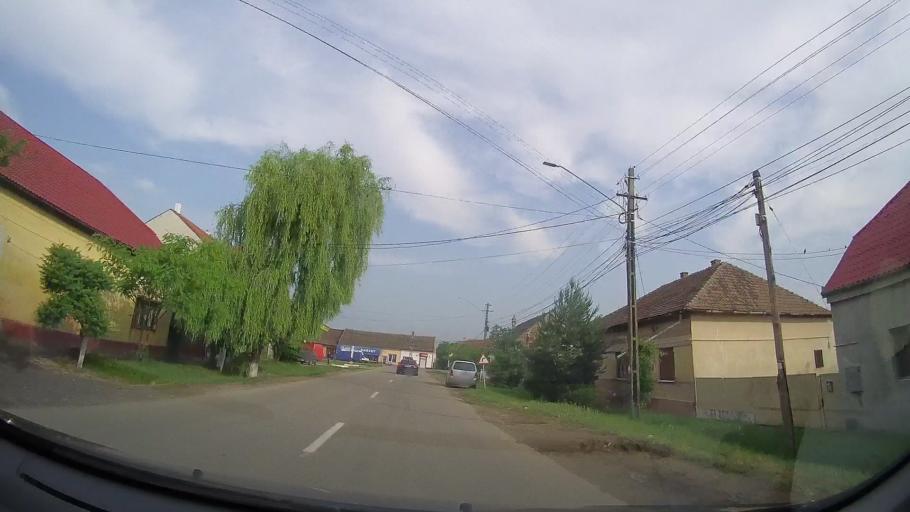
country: RO
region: Timis
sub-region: Comuna Peciu Nou
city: Peciu Nou
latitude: 45.6028
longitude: 21.0544
